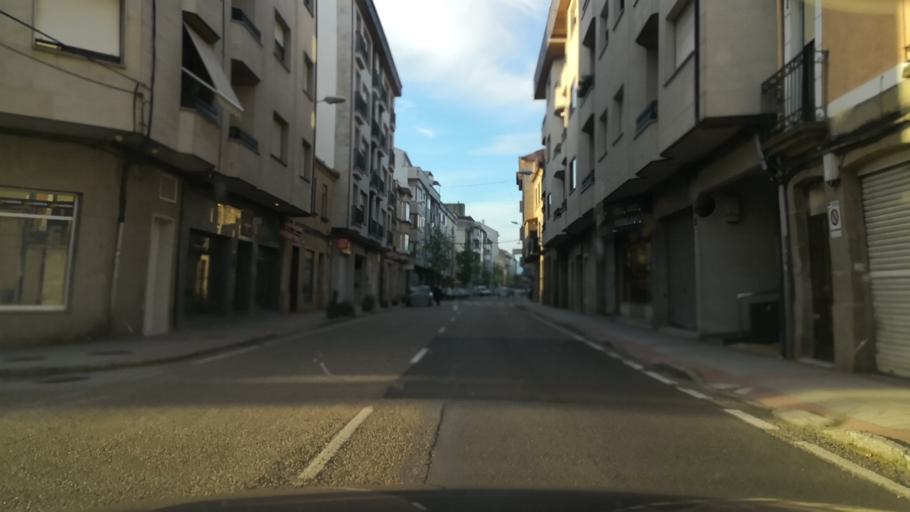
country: ES
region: Galicia
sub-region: Provincia de Ourense
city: Verin
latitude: 41.9364
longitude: -7.4385
